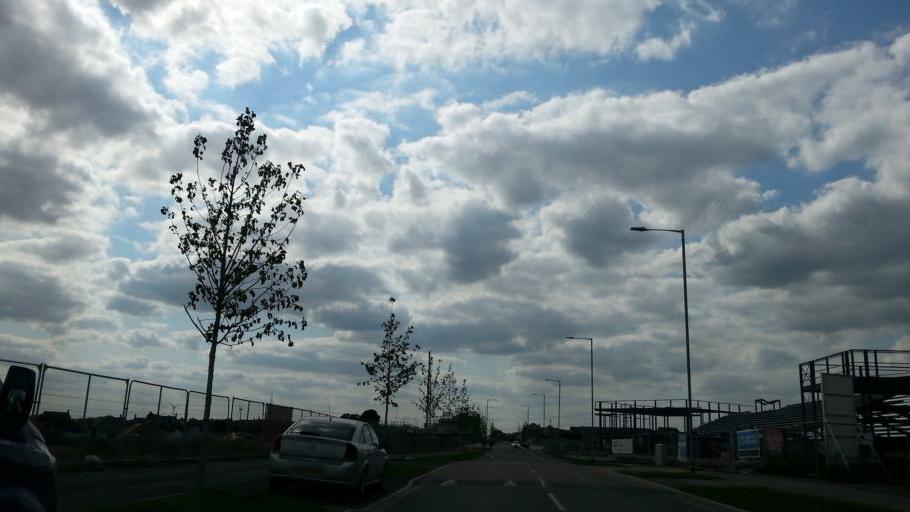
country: GB
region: England
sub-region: Leicestershire
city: Kirby Muxloe
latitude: 52.6142
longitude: -1.2200
